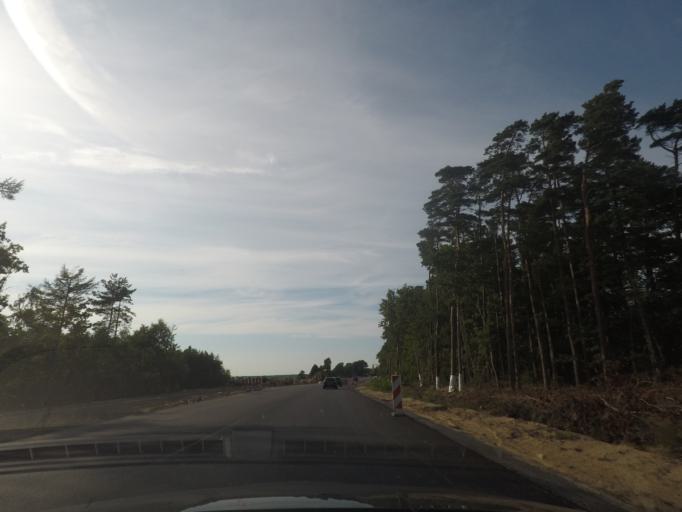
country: PL
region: Pomeranian Voivodeship
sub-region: Powiat leborski
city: Leba
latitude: 54.7338
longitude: 17.5611
